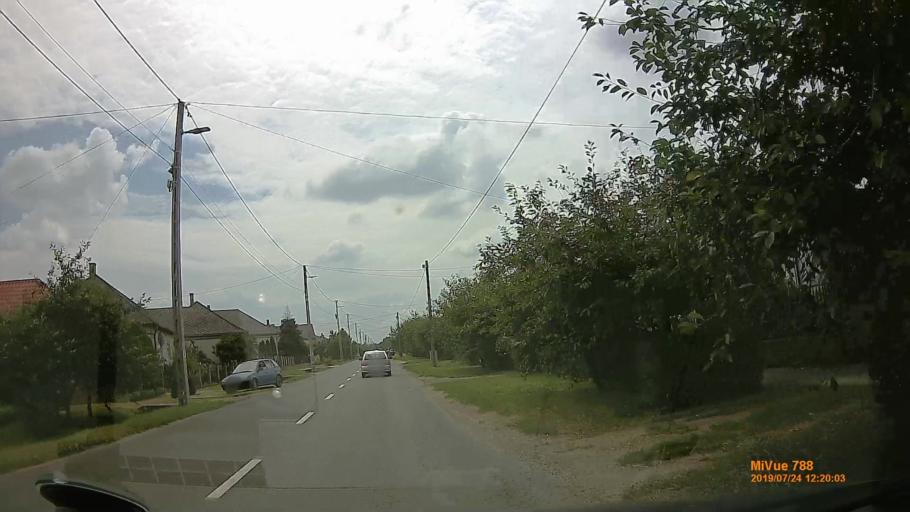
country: HU
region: Szabolcs-Szatmar-Bereg
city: Vasarosnameny
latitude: 48.1382
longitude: 22.3430
